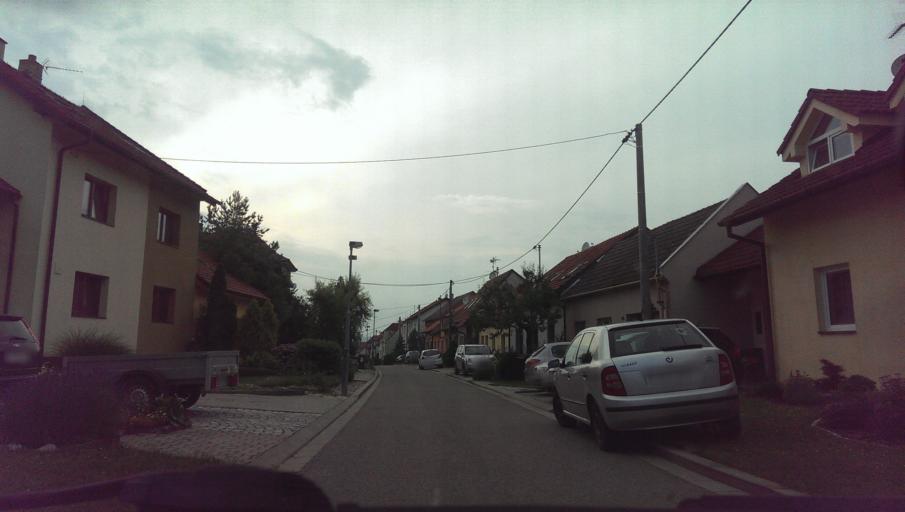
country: CZ
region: Zlin
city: Popovice
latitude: 49.0330
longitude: 17.5113
